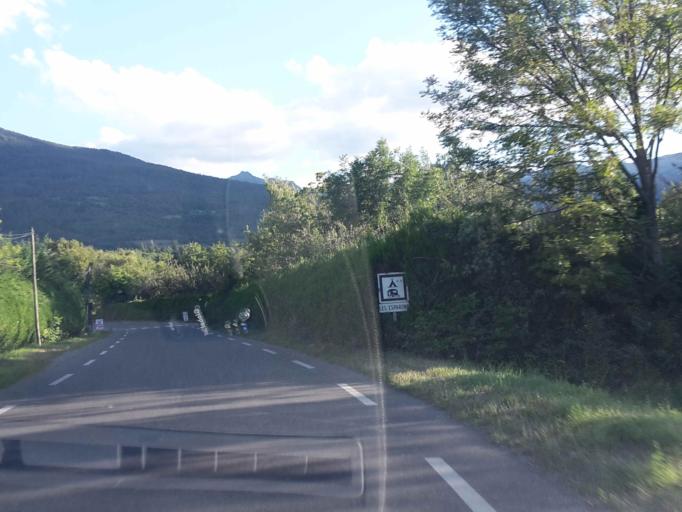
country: FR
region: Provence-Alpes-Cote d'Azur
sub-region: Departement des Hautes-Alpes
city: Embrun
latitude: 44.5454
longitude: 6.4983
